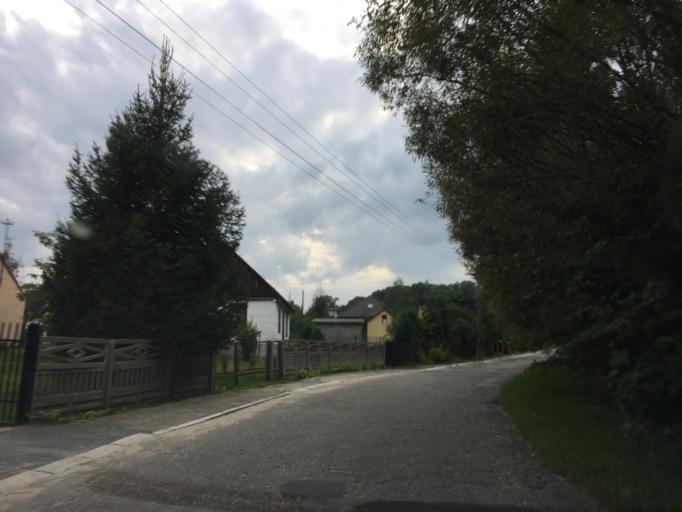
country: PL
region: Lodz Voivodeship
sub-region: Powiat radomszczanski
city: Przedborz
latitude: 51.1390
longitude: 19.8668
